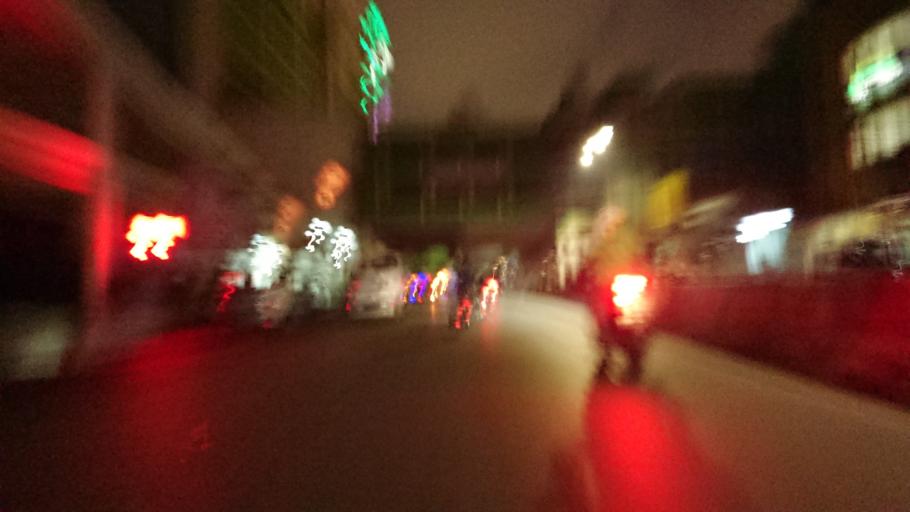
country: ID
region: Jakarta Raya
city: Jakarta
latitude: -6.1885
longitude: 106.8139
